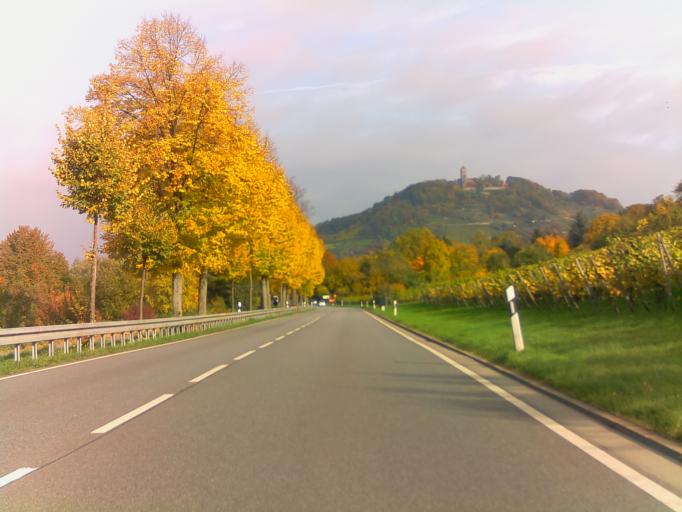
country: DE
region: Hesse
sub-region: Regierungsbezirk Darmstadt
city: Heppenheim an der Bergstrasse
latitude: 49.6284
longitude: 8.6416
